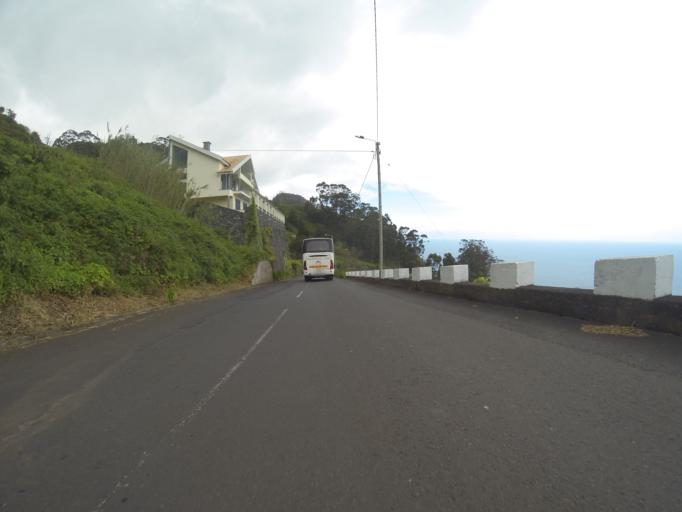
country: PT
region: Madeira
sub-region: Porto Moniz
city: Porto Moniz
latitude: 32.8624
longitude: -17.1735
